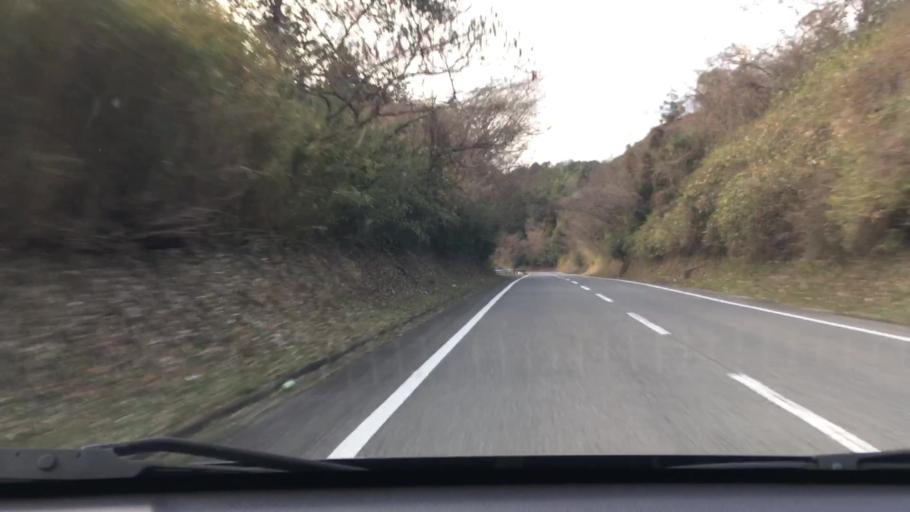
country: JP
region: Oita
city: Hiji
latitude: 33.4117
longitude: 131.4248
